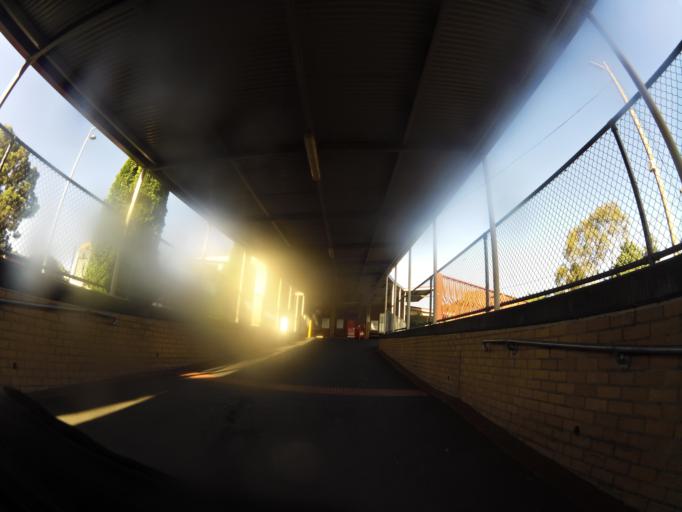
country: AU
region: Victoria
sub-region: Murrindindi
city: Kinglake West
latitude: -37.0248
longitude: 145.1375
